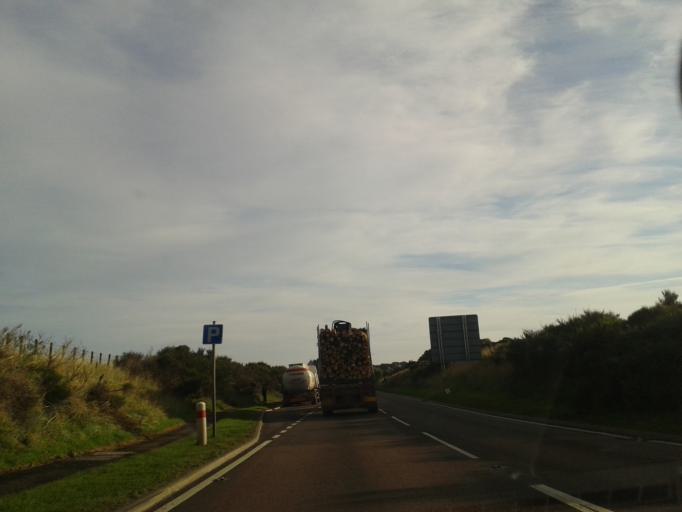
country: GB
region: Scotland
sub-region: Highland
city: Inverness
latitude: 57.4892
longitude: -4.1642
